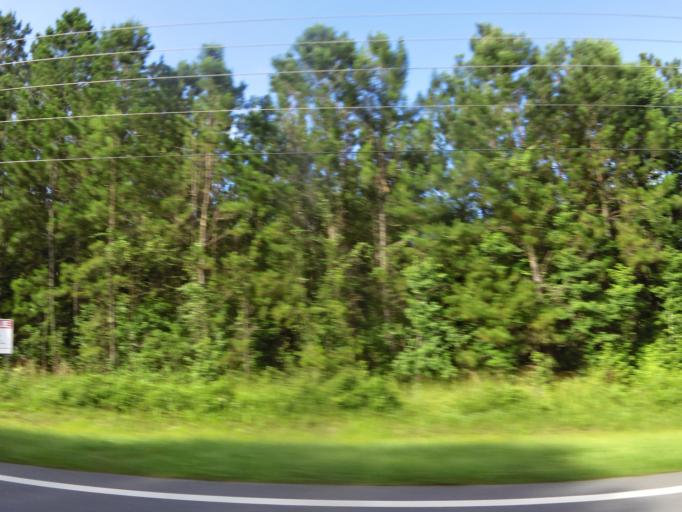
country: US
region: Florida
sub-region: Clay County
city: Green Cove Springs
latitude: 29.9946
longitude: -81.5376
